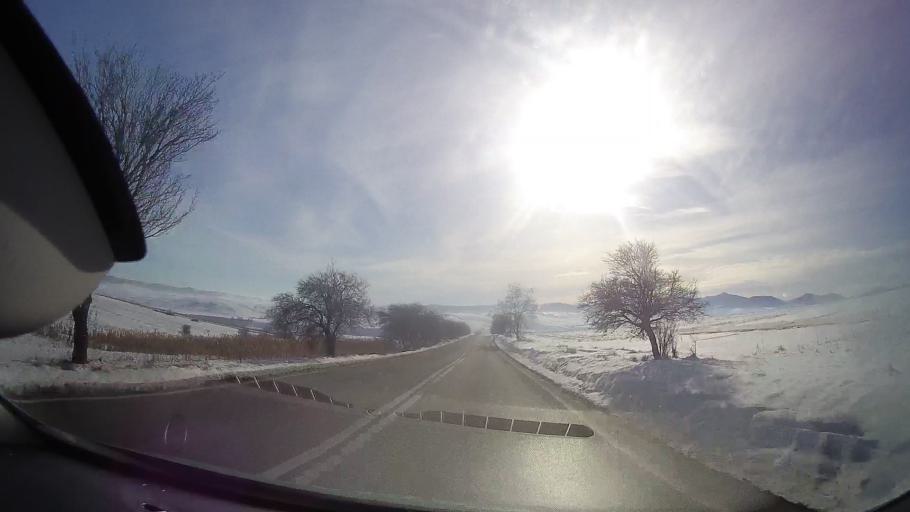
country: RO
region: Neamt
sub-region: Comuna Baltatesti
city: Valea Seaca
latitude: 47.1528
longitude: 26.3246
